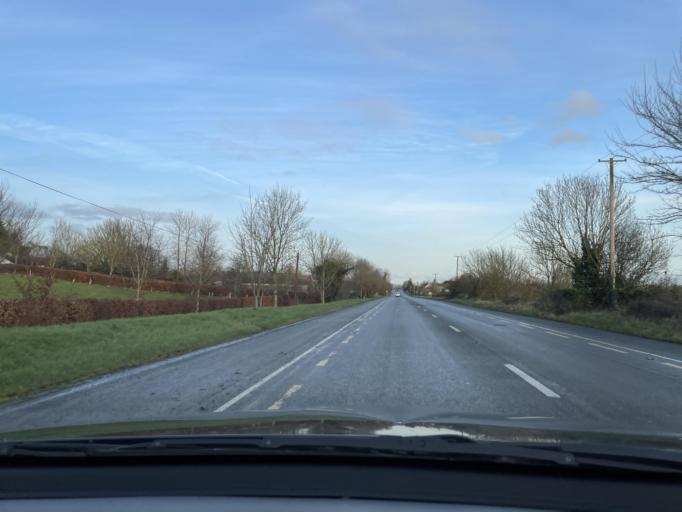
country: IE
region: Leinster
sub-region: Kilkenny
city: Thomastown
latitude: 52.6474
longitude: -7.1197
